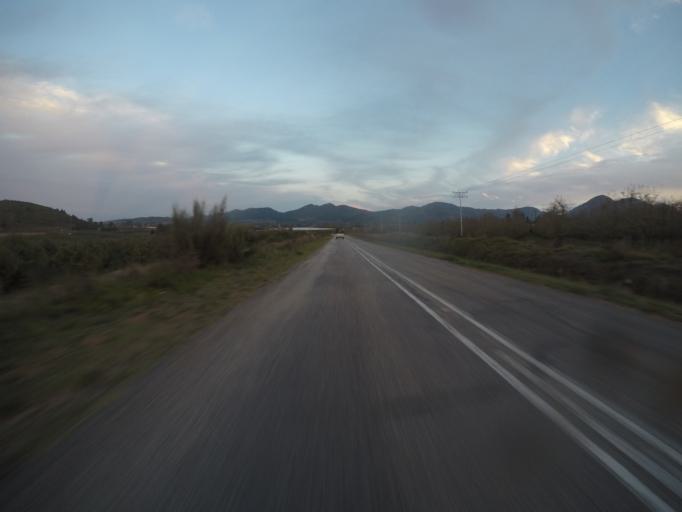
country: ZA
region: Western Cape
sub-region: Eden District Municipality
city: Plettenberg Bay
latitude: -33.7476
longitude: 23.4807
